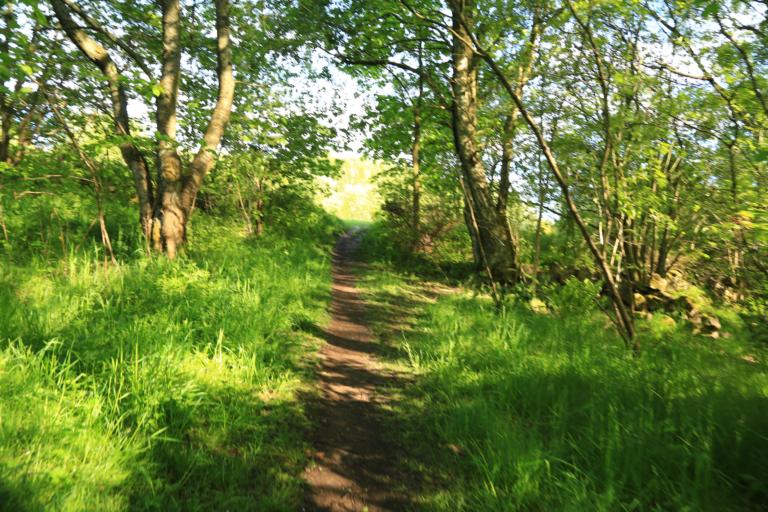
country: SE
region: Halland
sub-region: Varbergs Kommun
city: Traslovslage
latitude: 57.0968
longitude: 12.2868
